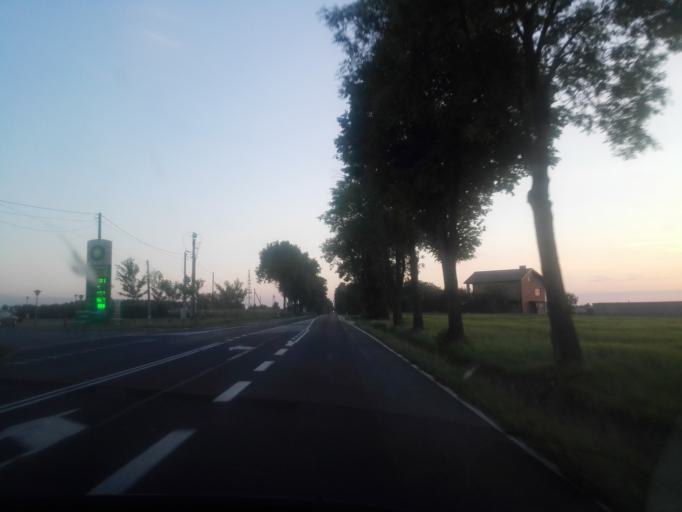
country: PL
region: Swietokrzyskie
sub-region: Powiat jedrzejowski
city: Slupia
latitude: 50.6448
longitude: 19.9192
